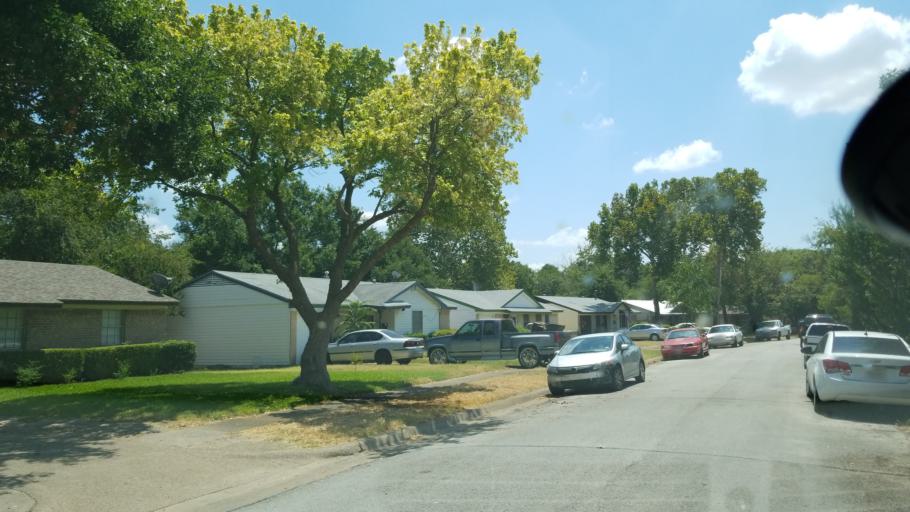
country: US
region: Texas
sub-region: Dallas County
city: Duncanville
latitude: 32.6707
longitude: -96.8983
